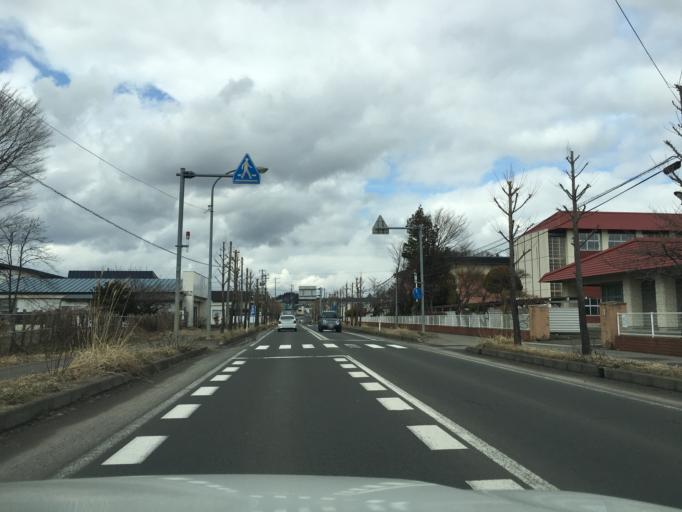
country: JP
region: Akita
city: Hanawa
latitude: 40.2656
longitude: 140.7700
